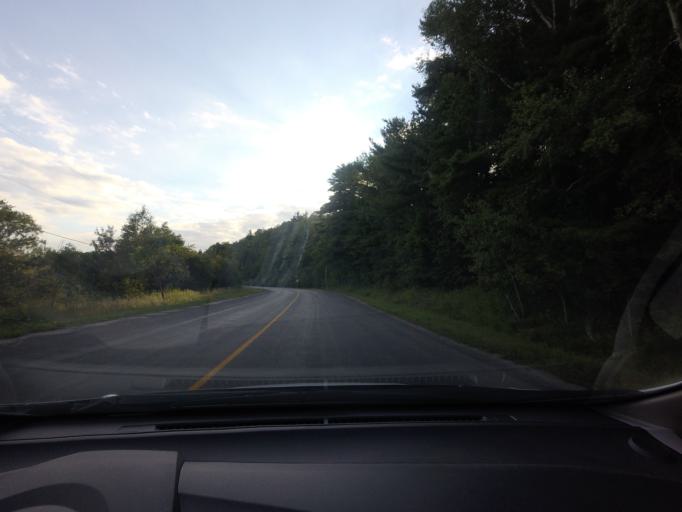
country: CA
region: Ontario
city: Perth
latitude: 44.6432
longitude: -76.5136
